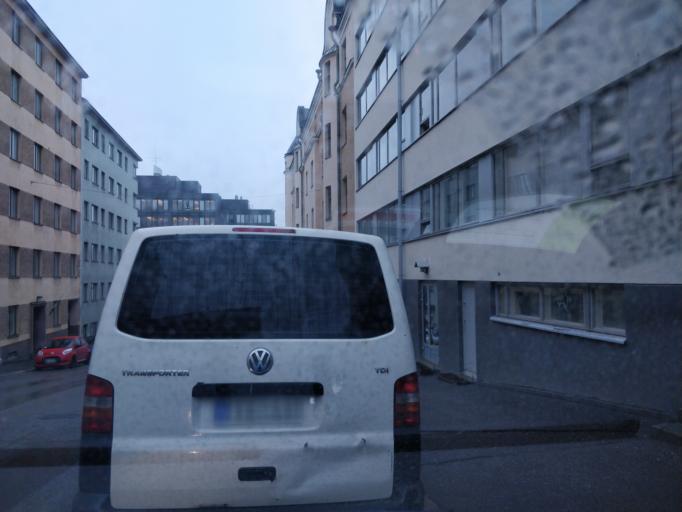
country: FI
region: Uusimaa
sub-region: Helsinki
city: Helsinki
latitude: 60.1886
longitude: 24.9560
